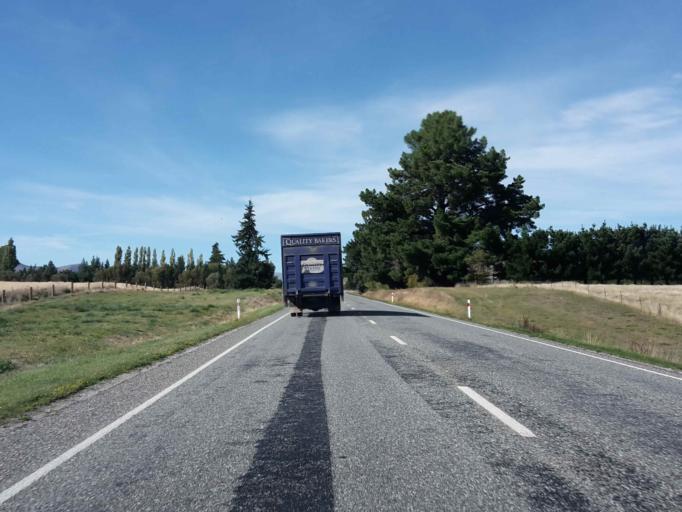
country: NZ
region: Otago
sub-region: Queenstown-Lakes District
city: Wanaka
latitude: -44.7143
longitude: 169.2116
